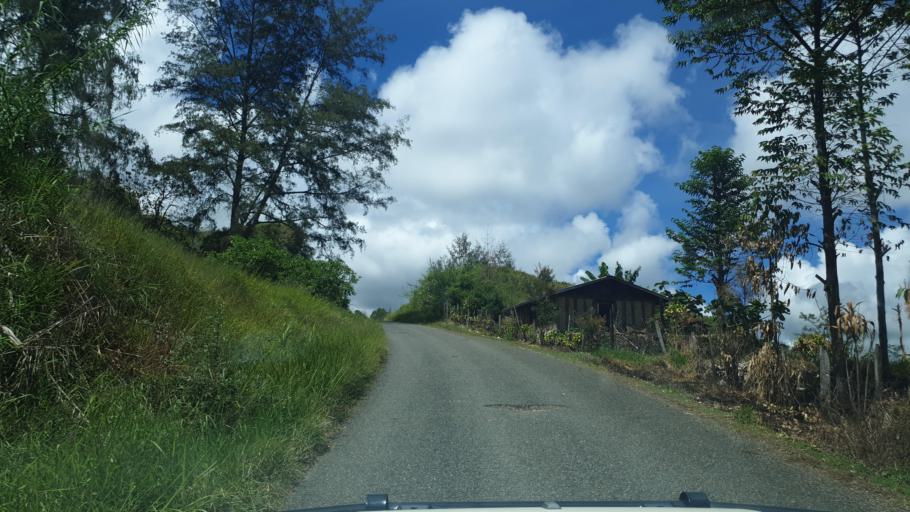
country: PG
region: Chimbu
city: Kundiawa
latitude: -6.1531
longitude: 145.1334
